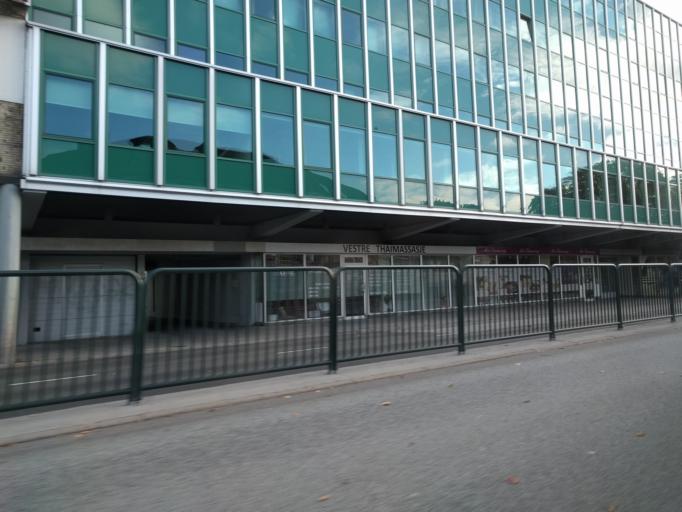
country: NO
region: Vest-Agder
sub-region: Kristiansand
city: Kristiansand
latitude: 58.1467
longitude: 7.9873
